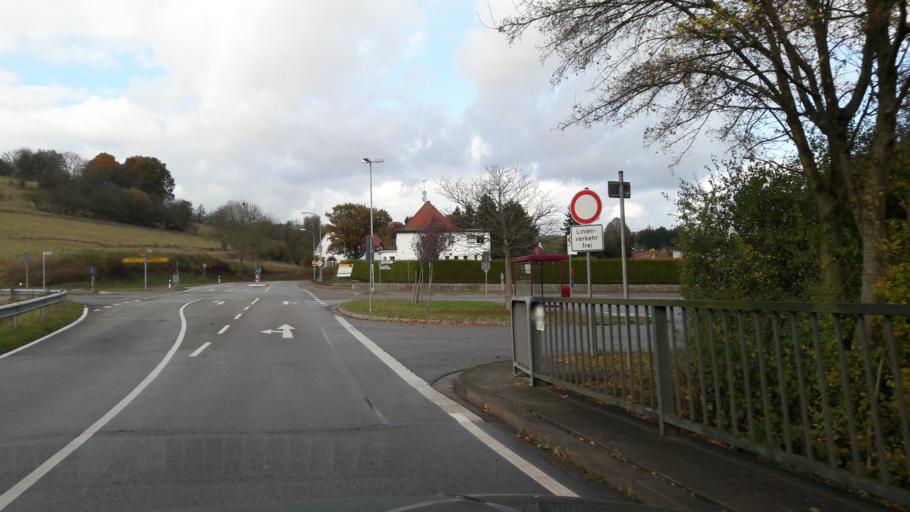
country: DE
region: Rheinland-Pfalz
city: Krottelbach
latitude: 49.4694
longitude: 7.3442
